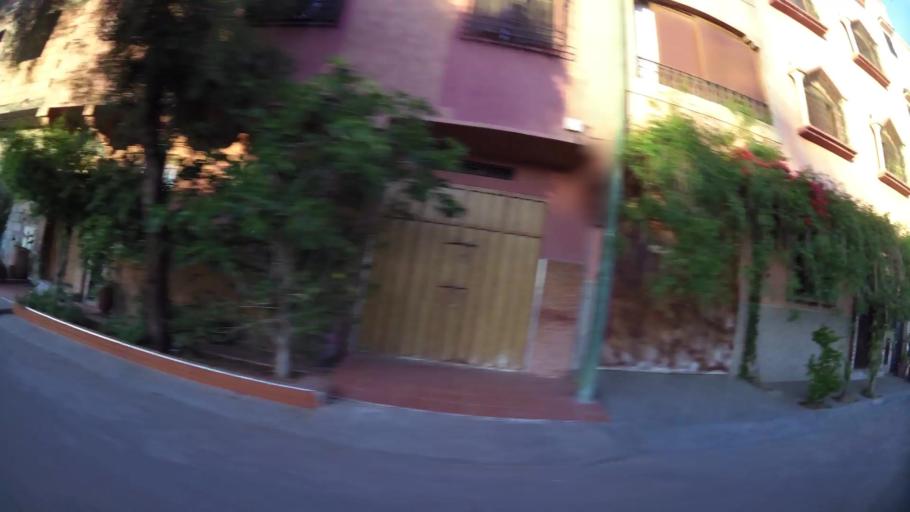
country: MA
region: Marrakech-Tensift-Al Haouz
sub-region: Marrakech
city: Marrakesh
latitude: 31.6362
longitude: -8.0375
